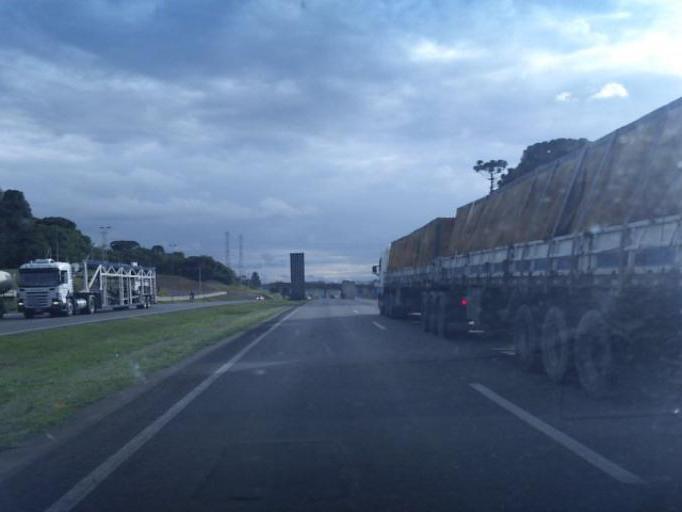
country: BR
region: Parana
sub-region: Sao Jose Dos Pinhais
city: Sao Jose dos Pinhais
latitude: -25.5173
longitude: -49.1323
